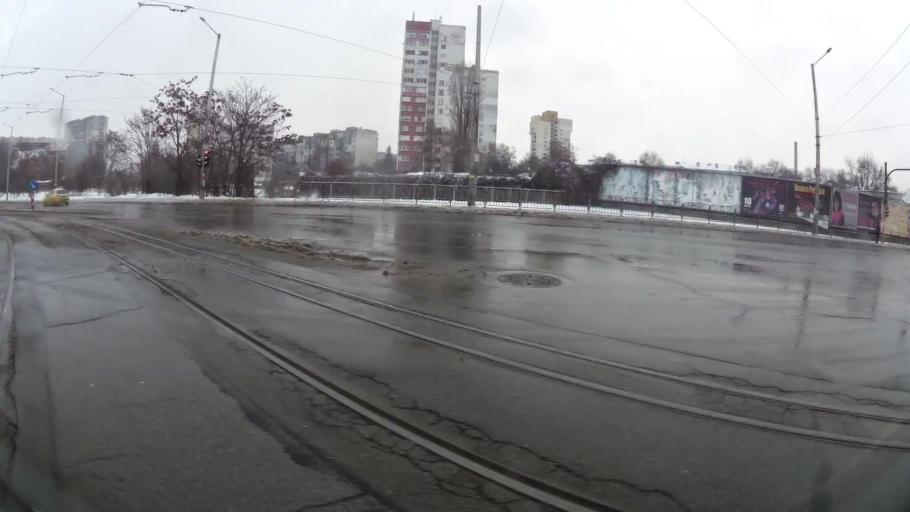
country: BG
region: Sofia-Capital
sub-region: Stolichna Obshtina
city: Sofia
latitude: 42.6943
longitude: 23.2948
